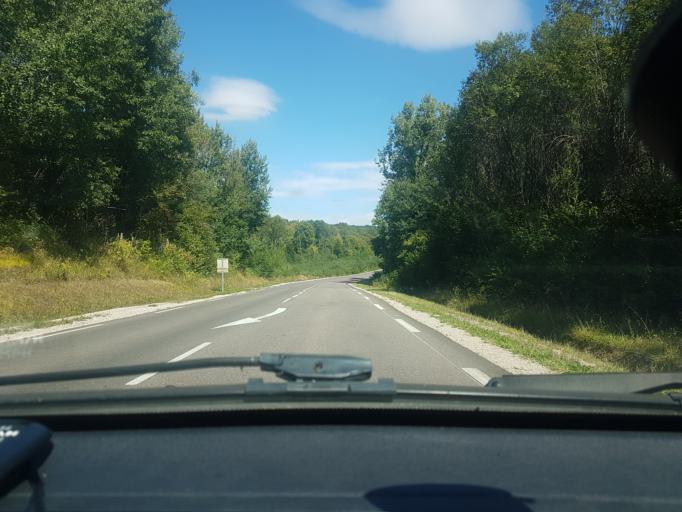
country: FR
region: Franche-Comte
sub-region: Departement de la Haute-Saone
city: Gray-la-Ville
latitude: 47.4080
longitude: 5.4950
